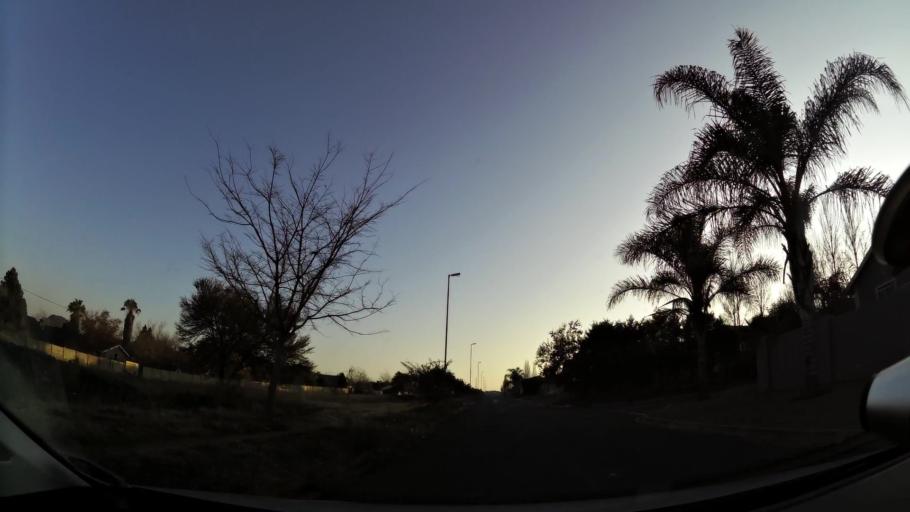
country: ZA
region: Orange Free State
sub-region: Mangaung Metropolitan Municipality
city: Bloemfontein
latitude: -29.0994
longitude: 26.1636
